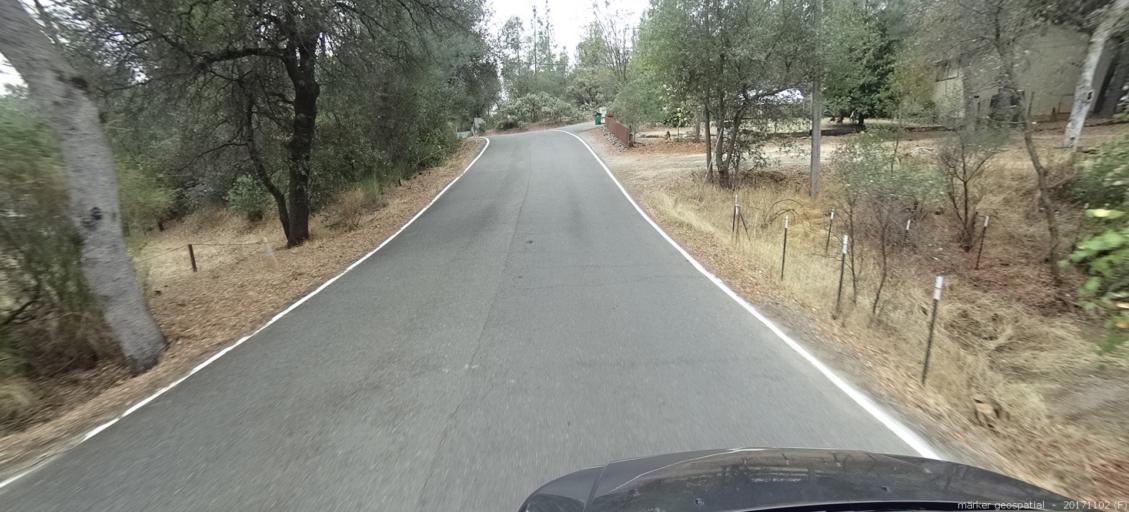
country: US
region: California
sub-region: Shasta County
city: Central Valley (historical)
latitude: 40.6406
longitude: -122.4021
